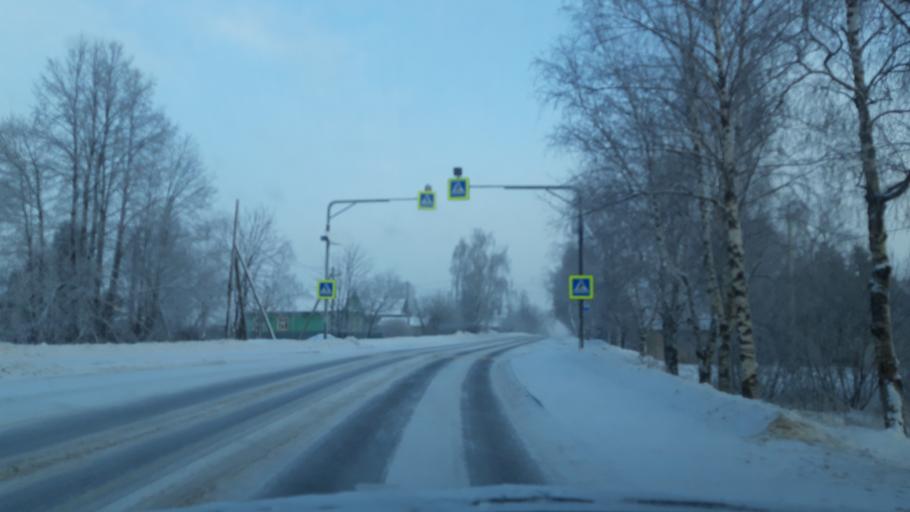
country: RU
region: Moskovskaya
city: Yakhroma
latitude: 56.3030
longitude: 37.4186
